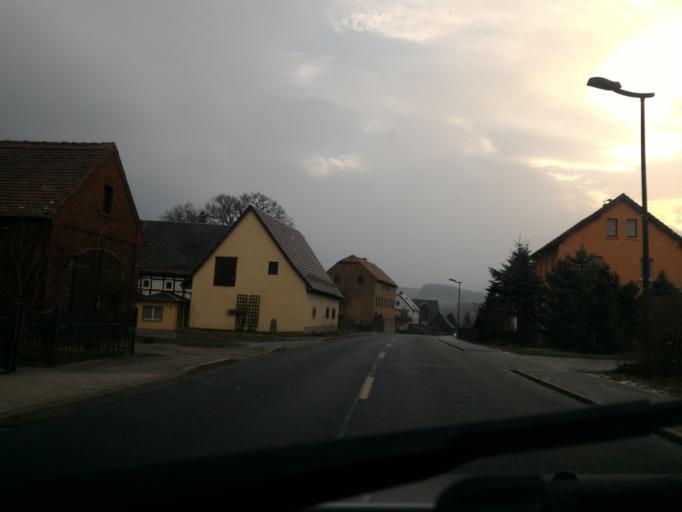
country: DE
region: Saxony
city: Grossschonau
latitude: 50.8932
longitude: 14.6778
